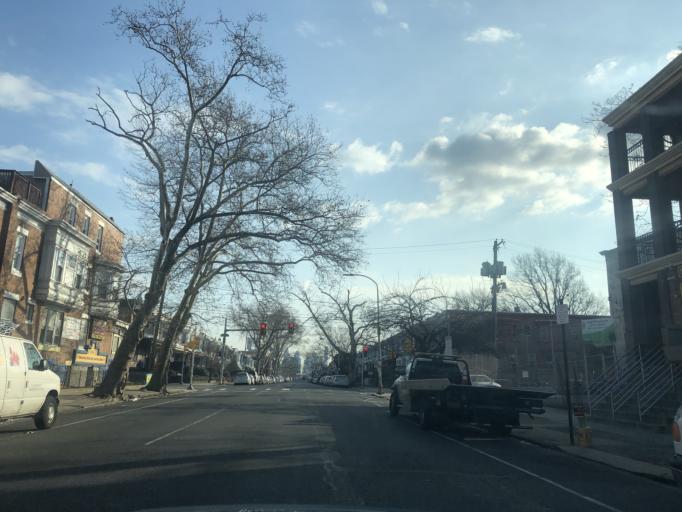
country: US
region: Pennsylvania
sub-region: Delaware County
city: Millbourne
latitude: 39.9583
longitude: -75.2239
